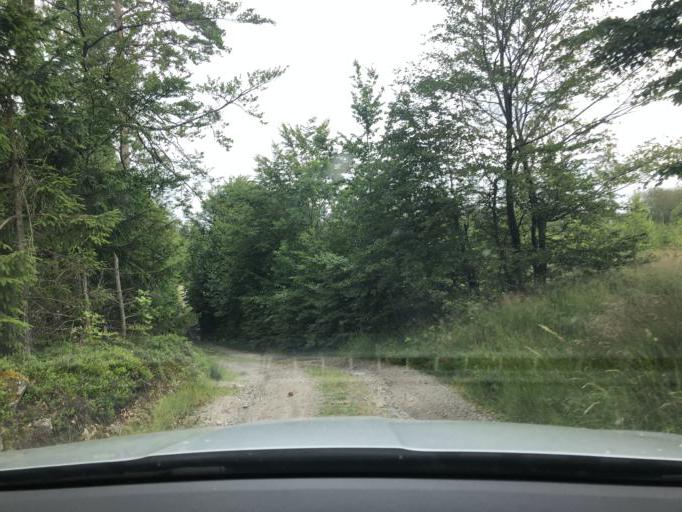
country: SE
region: Skane
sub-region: Bromolla Kommun
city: Nasum
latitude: 56.1558
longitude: 14.5771
